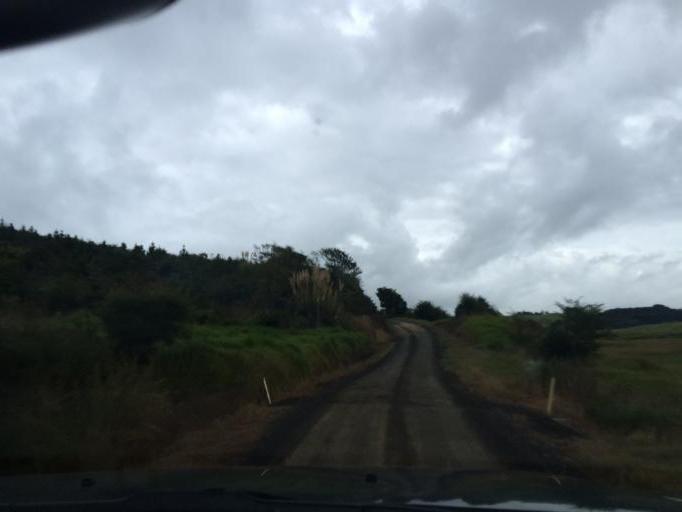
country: NZ
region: Northland
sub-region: Whangarei
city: Maungatapere
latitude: -35.8131
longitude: 174.0598
